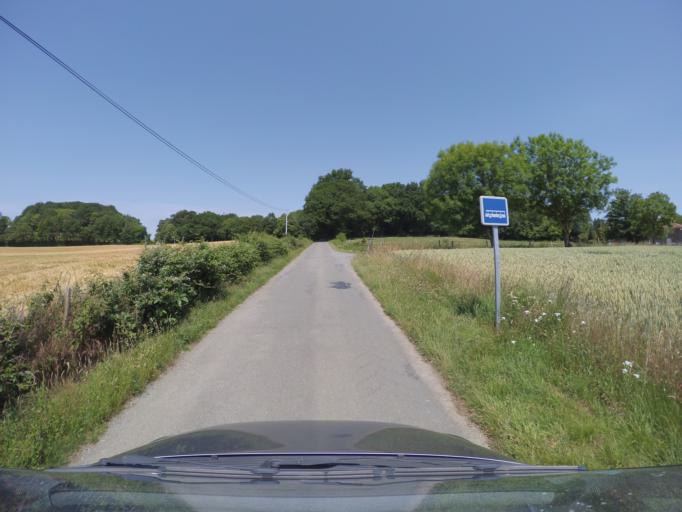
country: FR
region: Pays de la Loire
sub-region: Departement de la Vendee
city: La Flocelliere
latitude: 46.8150
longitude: -0.8506
